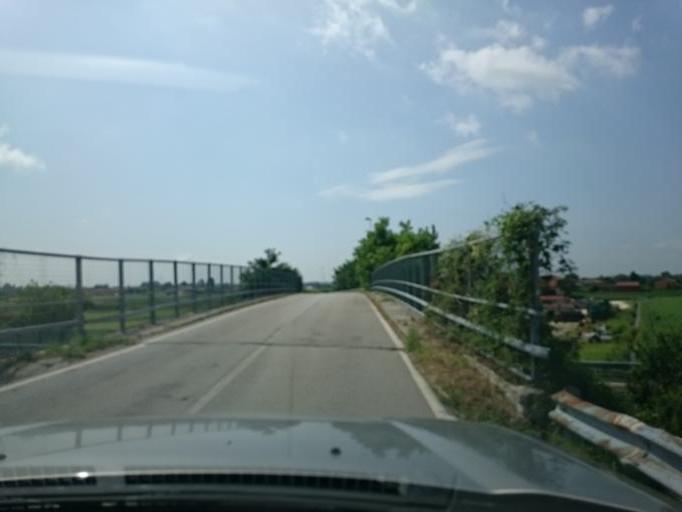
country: IT
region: Veneto
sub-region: Provincia di Padova
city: Masera di Padova
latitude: 45.3394
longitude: 11.8520
